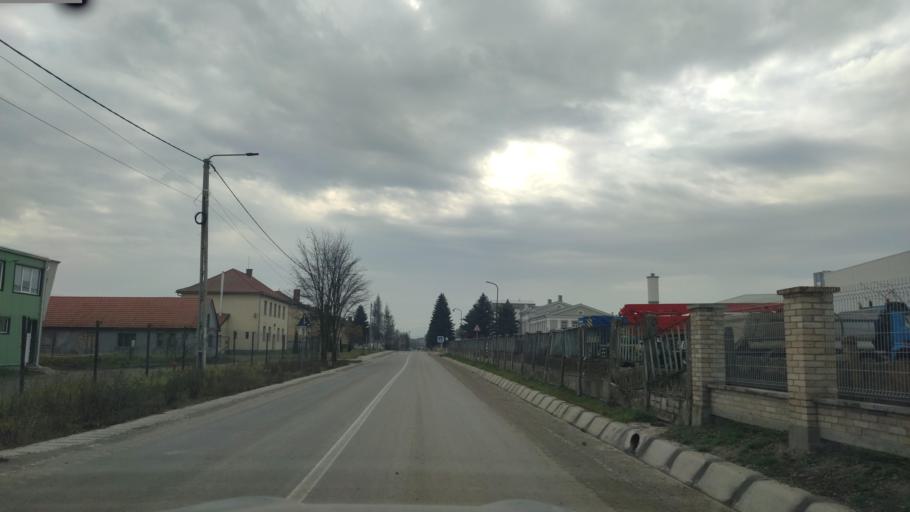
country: RO
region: Harghita
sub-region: Comuna Remetea
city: Remetea
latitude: 46.8148
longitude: 25.4604
